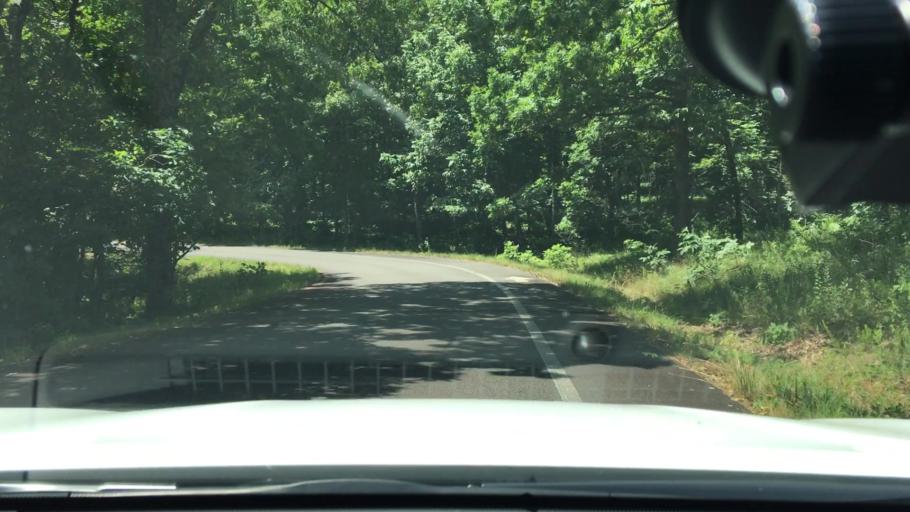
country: US
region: Arkansas
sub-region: Logan County
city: Paris
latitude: 35.1753
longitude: -93.6431
